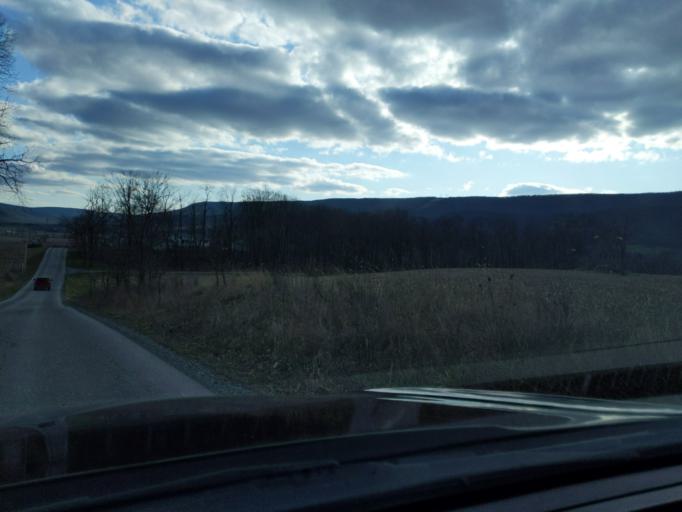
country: US
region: Pennsylvania
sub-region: Blair County
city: Tipton
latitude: 40.5869
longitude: -78.2574
